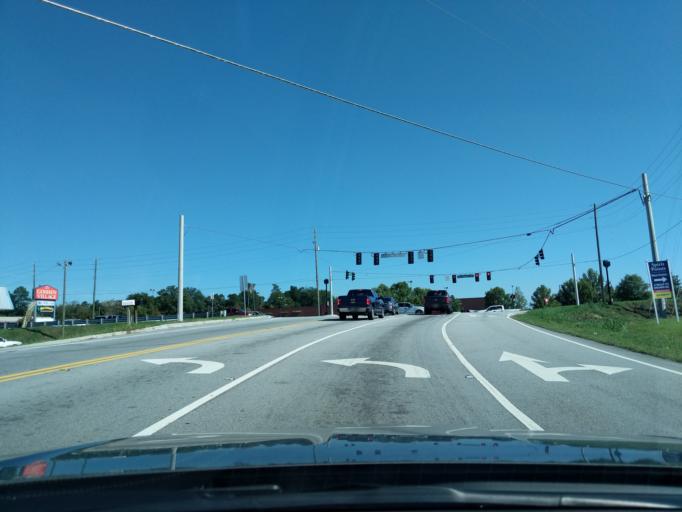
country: US
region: Georgia
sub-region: Richmond County
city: Augusta
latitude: 33.3658
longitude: -81.9962
